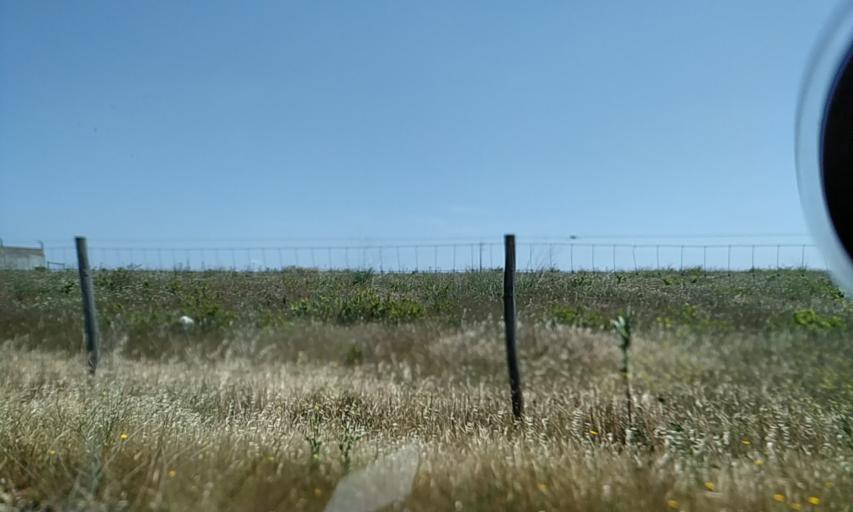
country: PT
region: Setubal
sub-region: Palmela
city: Palmela
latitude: 38.6010
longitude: -8.8271
